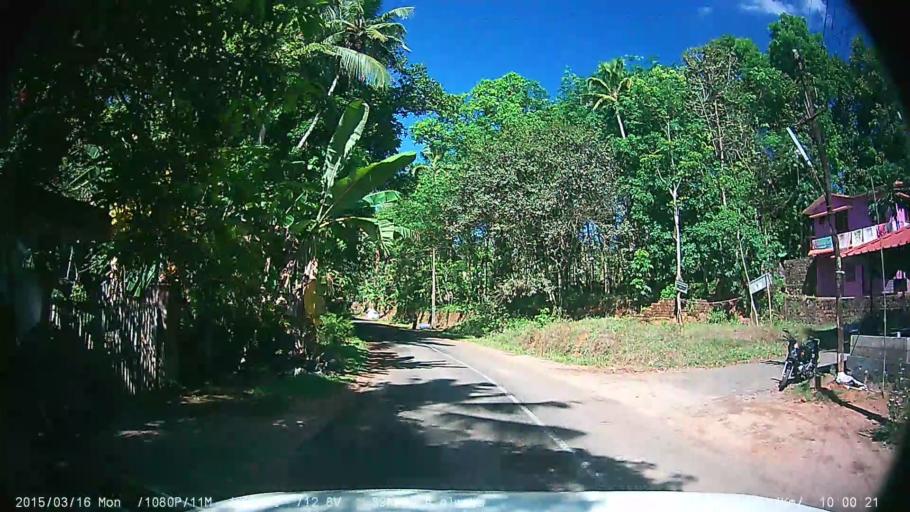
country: IN
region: Kerala
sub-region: Kottayam
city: Palackattumala
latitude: 9.7821
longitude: 76.5897
